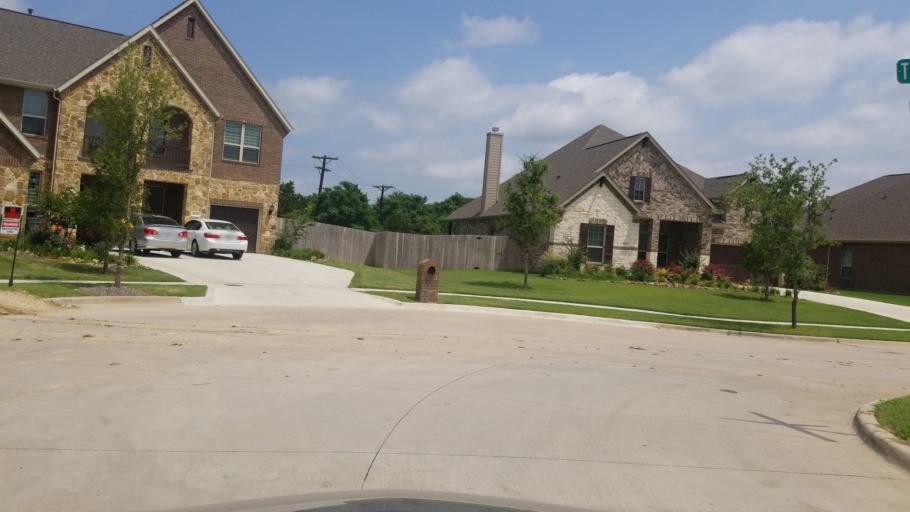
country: US
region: Texas
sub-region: Dallas County
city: Duncanville
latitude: 32.6831
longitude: -96.9389
